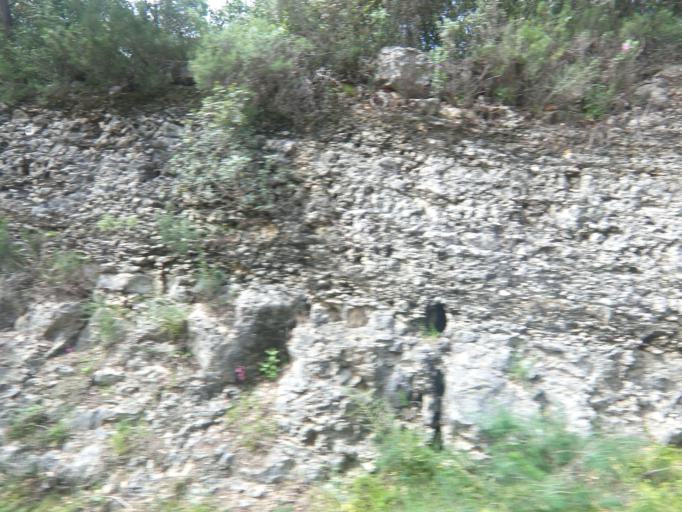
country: PT
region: Setubal
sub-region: Setubal
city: Setubal
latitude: 38.4915
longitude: -8.9379
